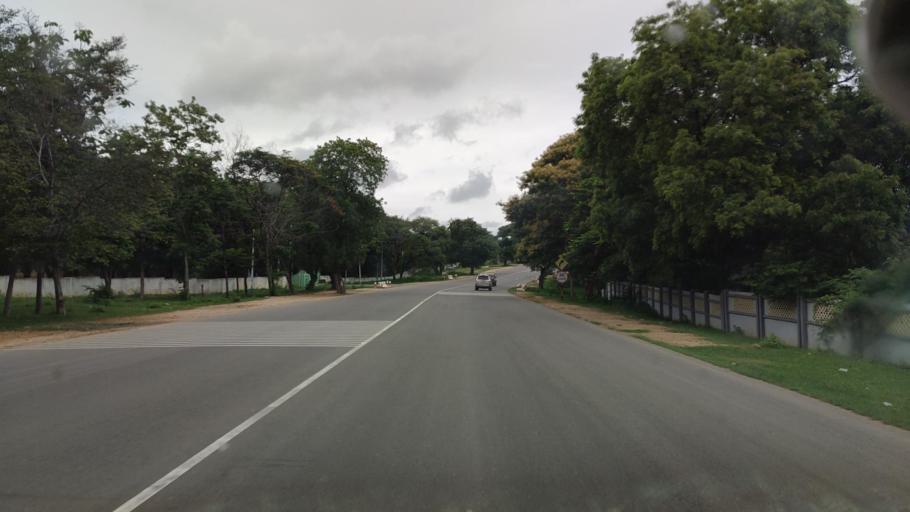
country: MM
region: Mandalay
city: Meiktila
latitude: 20.8575
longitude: 95.8721
